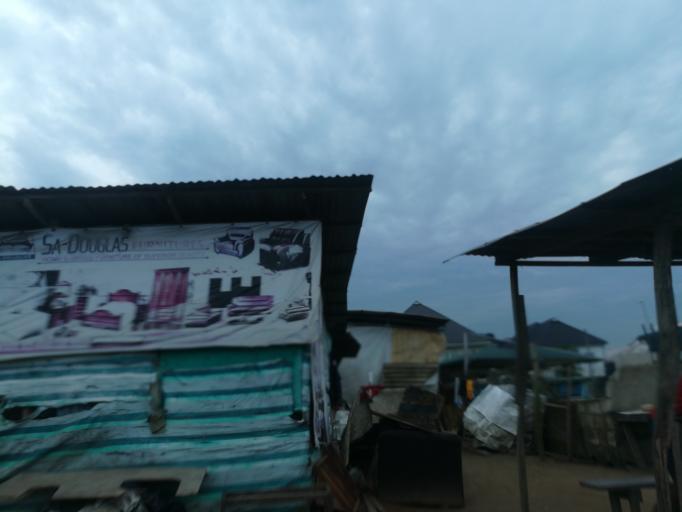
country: NG
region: Rivers
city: Port Harcourt
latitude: 4.8028
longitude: 6.9532
